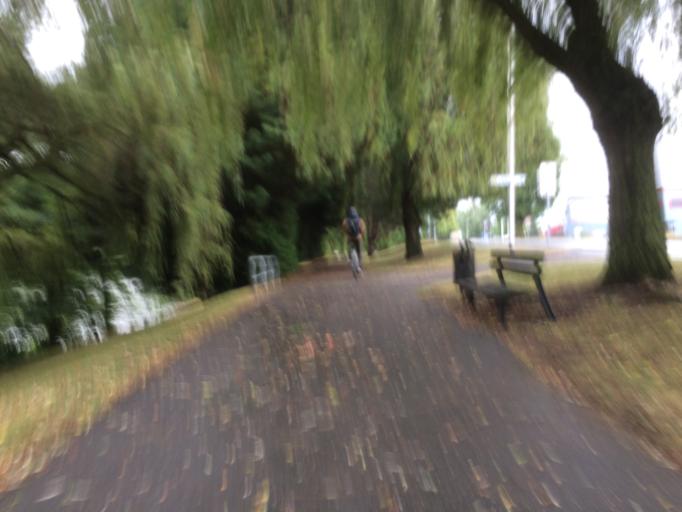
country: FR
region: Picardie
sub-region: Departement de l'Oise
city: Jaux
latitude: 49.3952
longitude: 2.7841
